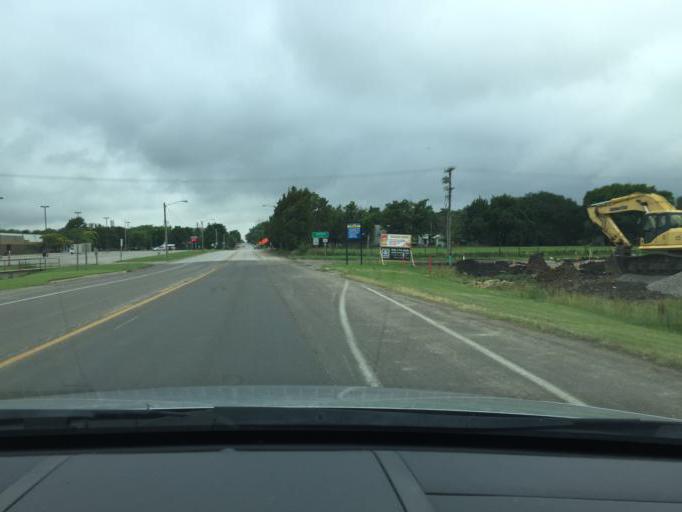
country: US
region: Kansas
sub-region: McPherson County
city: Moundridge
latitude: 38.2031
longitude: -97.5091
